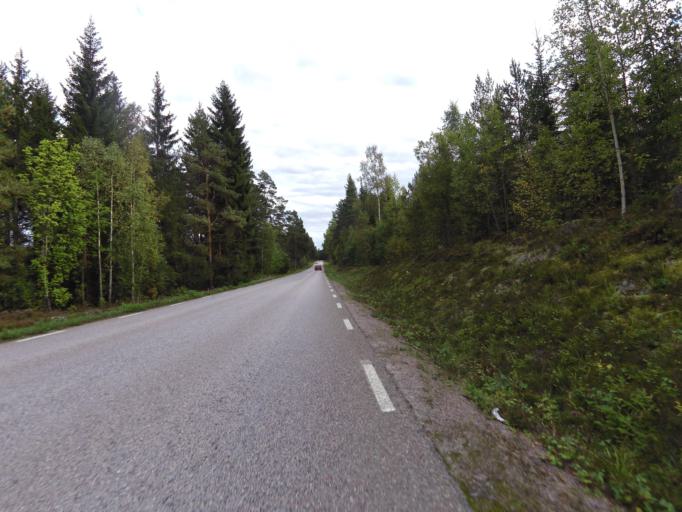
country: SE
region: Gaevleborg
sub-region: Gavle Kommun
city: Valbo
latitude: 60.6635
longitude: 16.9598
